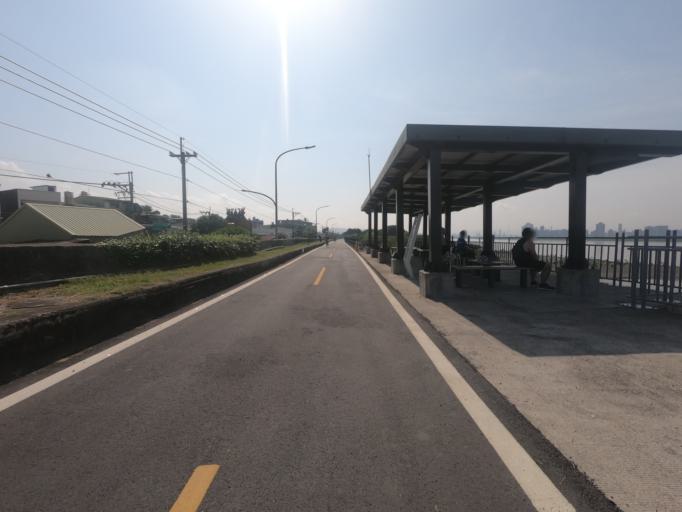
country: TW
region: Taipei
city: Taipei
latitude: 25.1061
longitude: 121.4726
